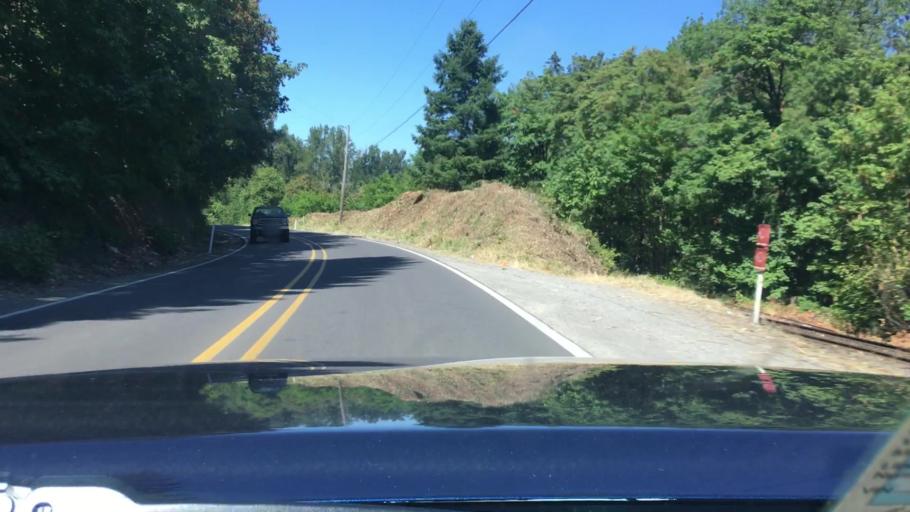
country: US
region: Oregon
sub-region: Lane County
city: Cottage Grove
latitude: 43.8138
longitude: -123.0461
